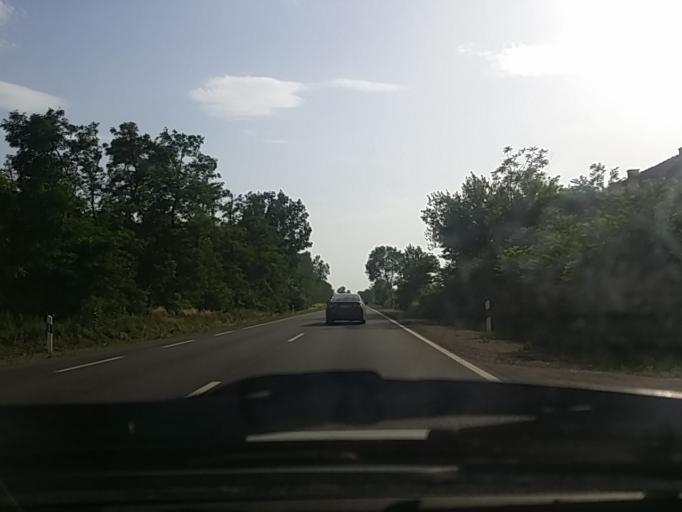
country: HU
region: Pest
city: Farmos
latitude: 47.4534
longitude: 19.8301
